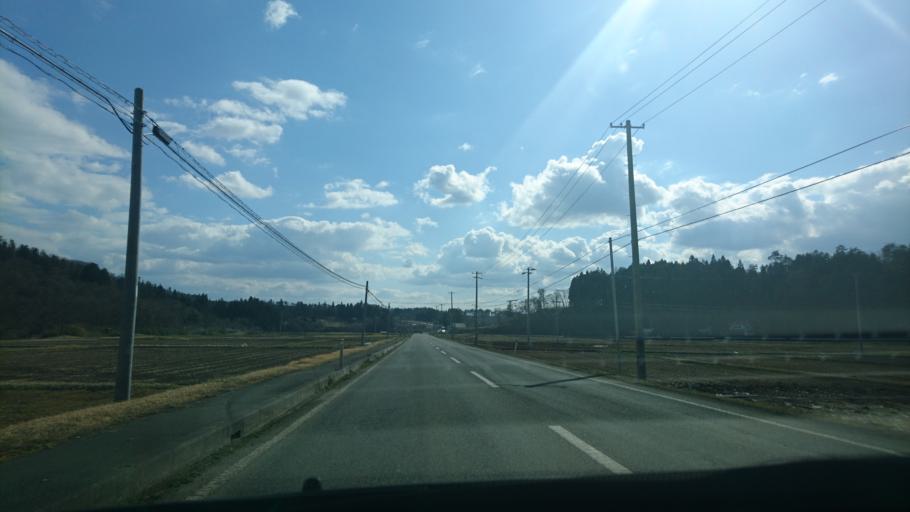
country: JP
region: Iwate
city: Kitakami
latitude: 39.2391
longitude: 141.1981
